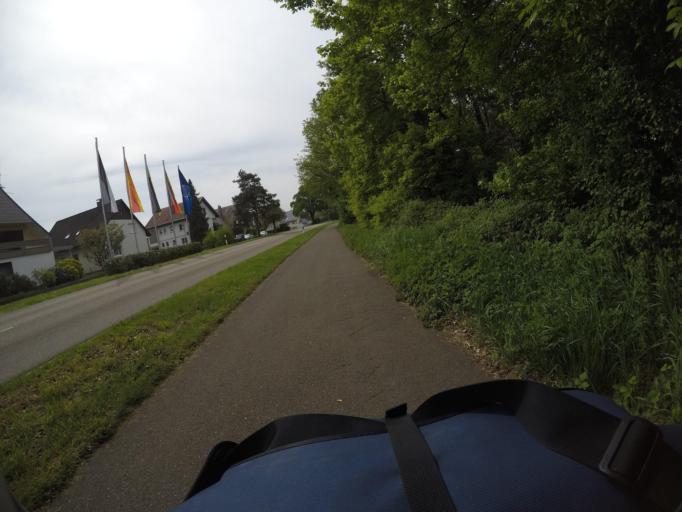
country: DE
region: Baden-Wuerttemberg
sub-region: Karlsruhe Region
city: Iffezheim
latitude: 48.8155
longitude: 8.1430
